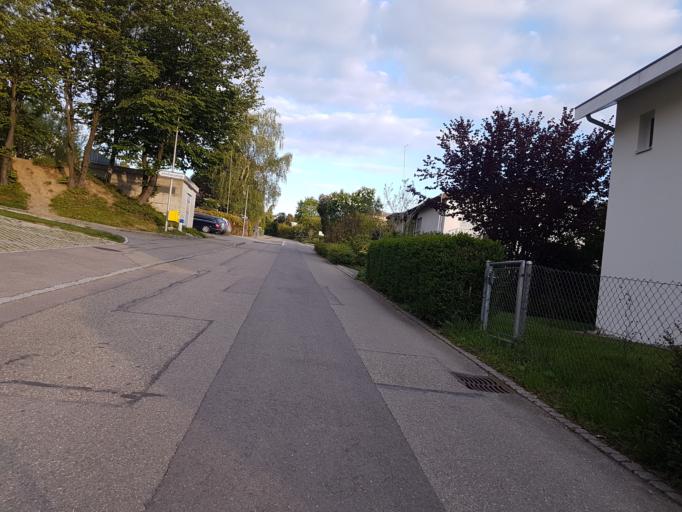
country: CH
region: Bern
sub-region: Biel/Bienne District
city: Bellmund
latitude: 47.1122
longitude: 7.2347
